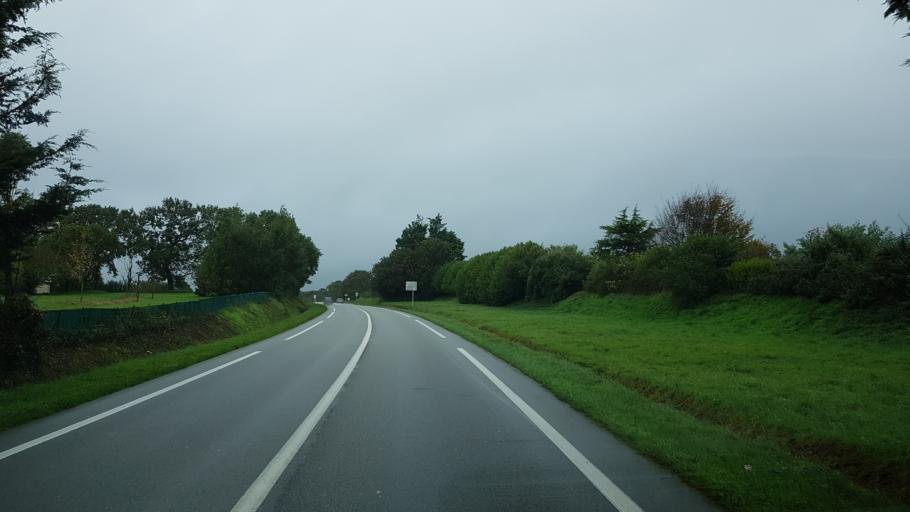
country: FR
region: Brittany
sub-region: Departement du Morbihan
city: Theix
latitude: 47.6184
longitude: -2.6854
